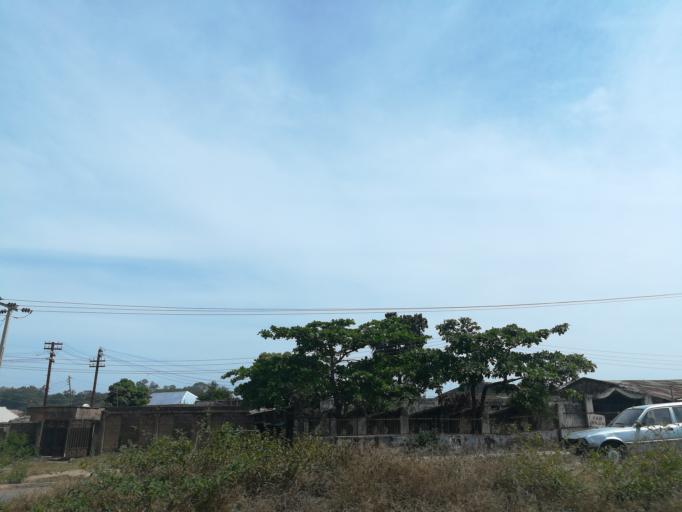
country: NG
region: Plateau
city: Bukuru
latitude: 9.8022
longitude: 8.8603
